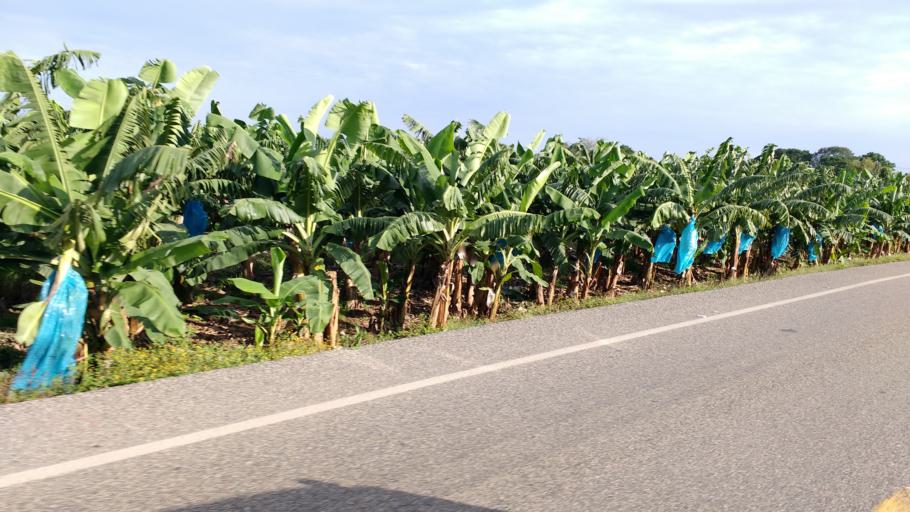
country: MX
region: Tabasco
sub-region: Teapa
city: Eureka y Belen
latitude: 17.6215
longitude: -92.9628
